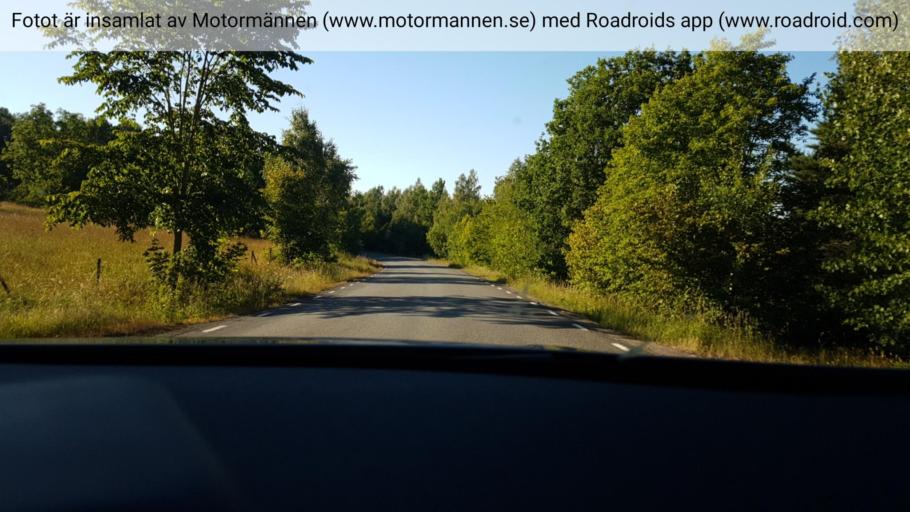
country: SE
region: Vaestra Goetaland
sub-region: Tidaholms Kommun
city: Tidaholm
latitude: 58.1146
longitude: 14.0725
